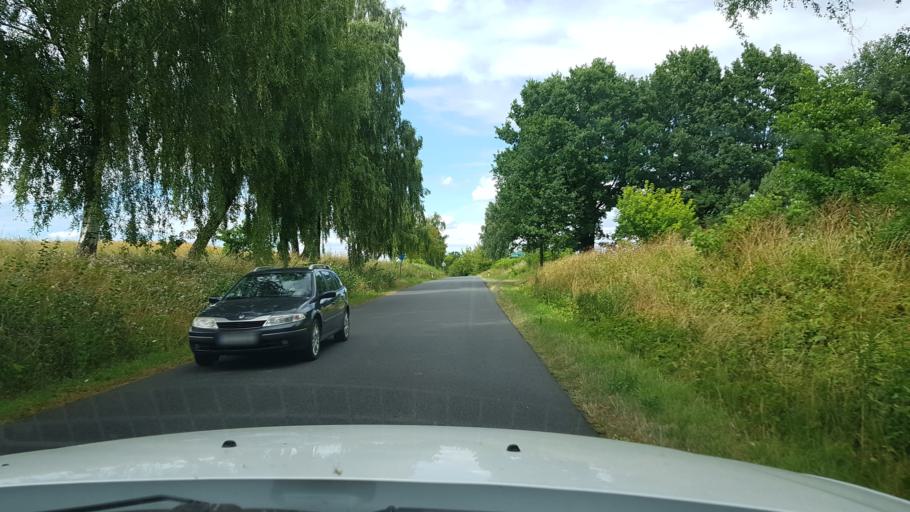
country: PL
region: West Pomeranian Voivodeship
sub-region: Powiat drawski
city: Kalisz Pomorski
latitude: 53.3163
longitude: 15.9207
